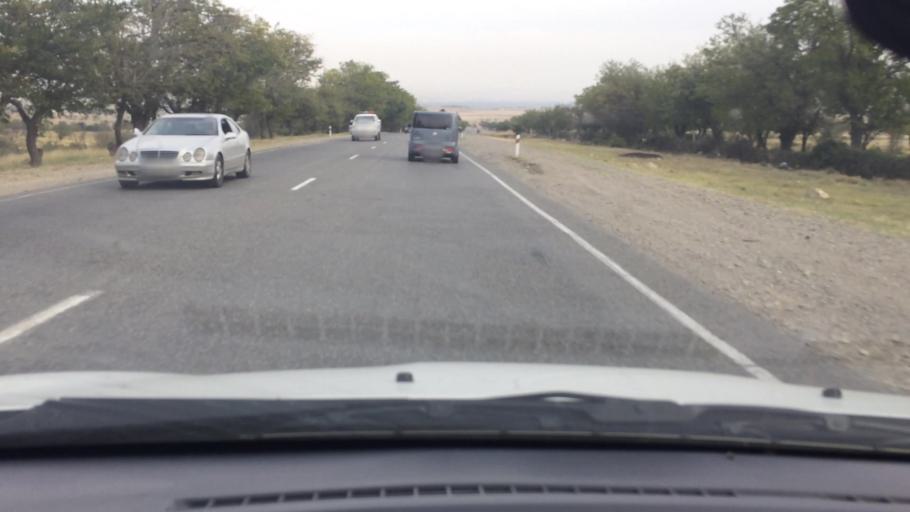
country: GE
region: T'bilisi
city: Tbilisi
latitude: 41.6414
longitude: 44.8618
